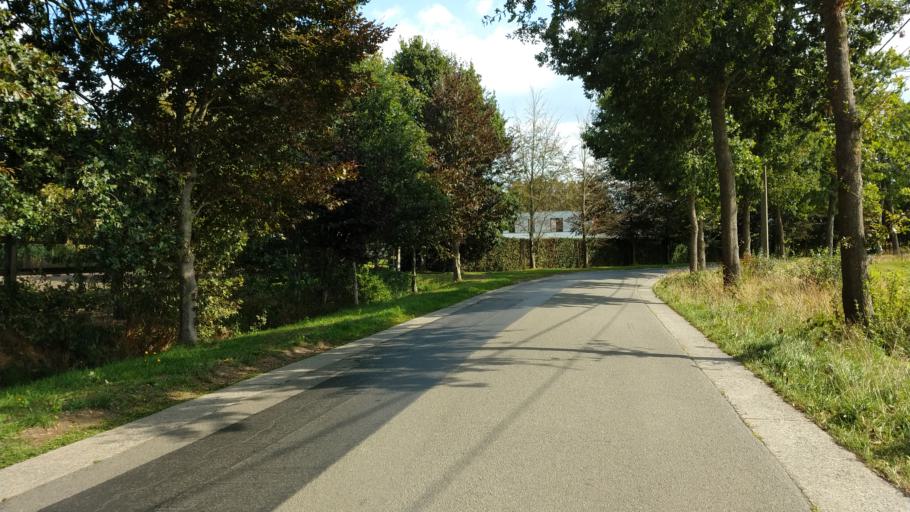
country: BE
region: Flanders
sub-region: Provincie Oost-Vlaanderen
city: Evergem
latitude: 51.1791
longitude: 3.6835
